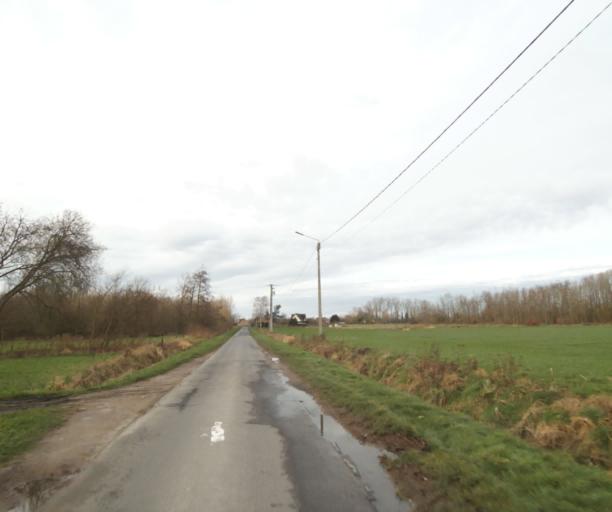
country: FR
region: Nord-Pas-de-Calais
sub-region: Departement du Nord
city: Vieux-Conde
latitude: 50.4869
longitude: 3.5663
